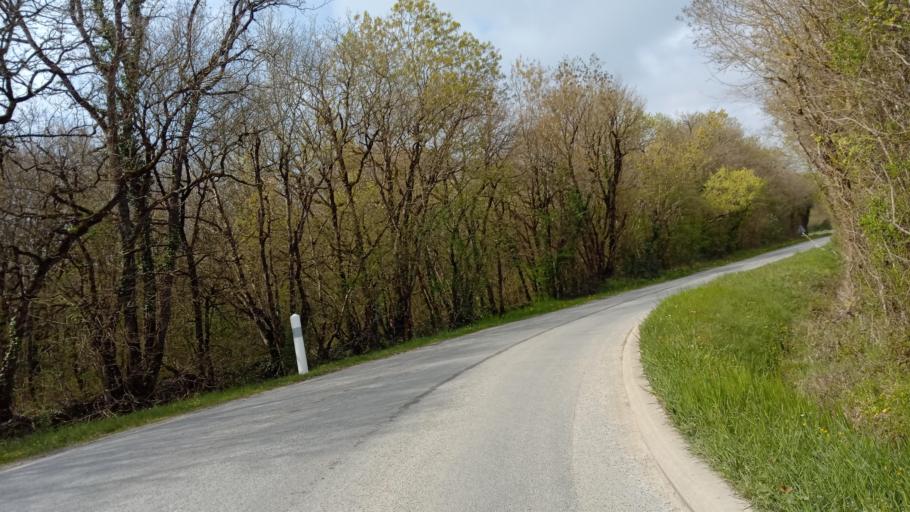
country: FR
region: Poitou-Charentes
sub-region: Departement de la Charente-Maritime
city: Verines
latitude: 46.1478
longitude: -0.9365
